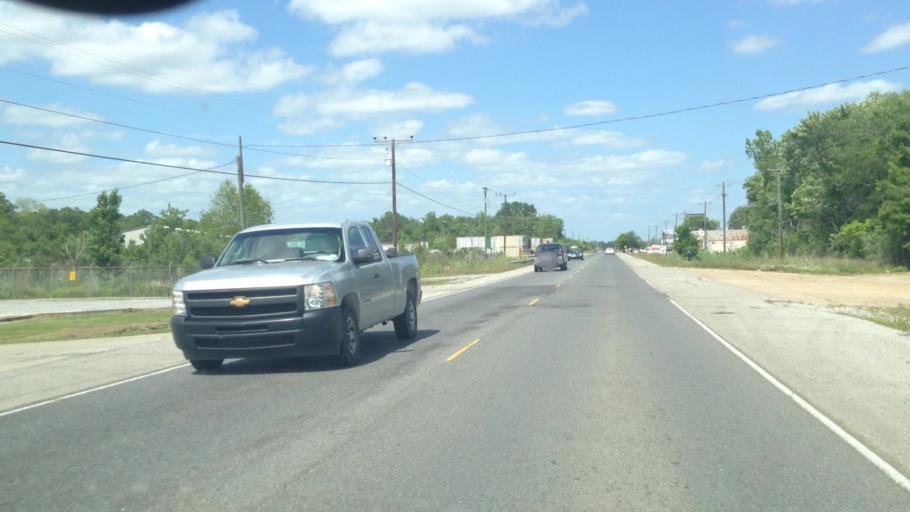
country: US
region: Louisiana
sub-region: Terrebonne Parish
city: Houma
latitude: 29.6494
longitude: -90.6842
